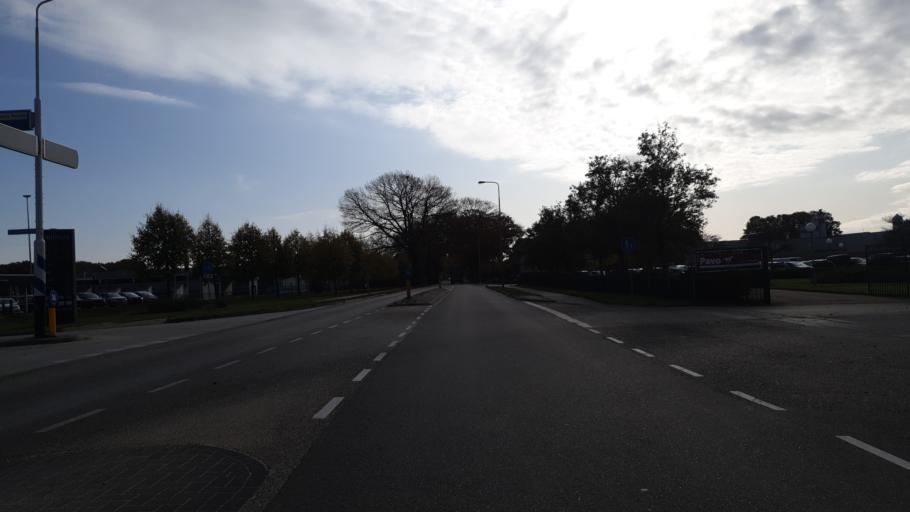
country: NL
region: Limburg
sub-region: Gemeente Gennep
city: Gennep
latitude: 51.6822
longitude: 5.9746
